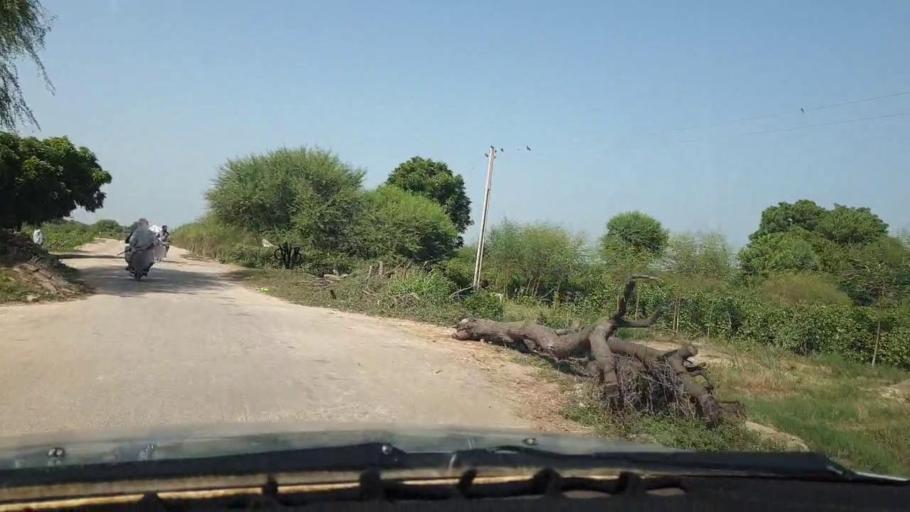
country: PK
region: Sindh
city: Chambar
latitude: 25.2282
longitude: 68.8695
